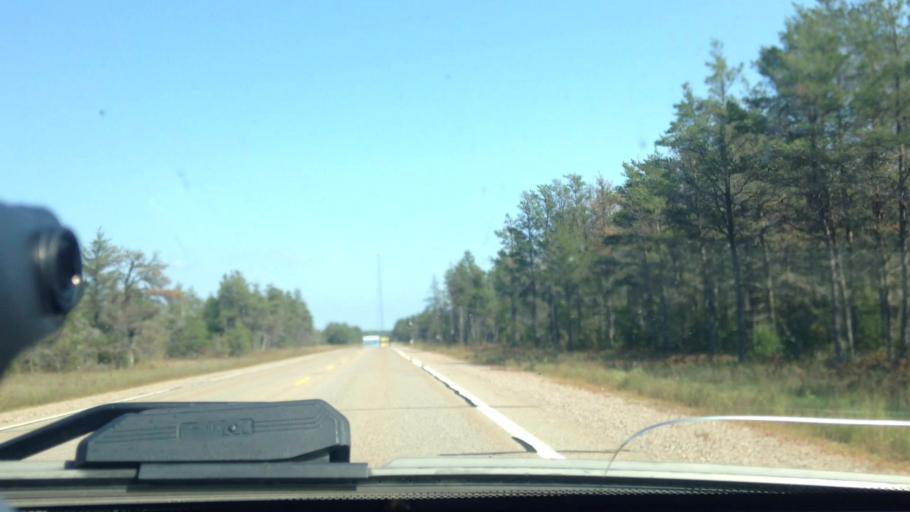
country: US
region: Michigan
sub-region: Chippewa County
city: Sault Ste. Marie
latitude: 46.3588
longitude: -84.8080
